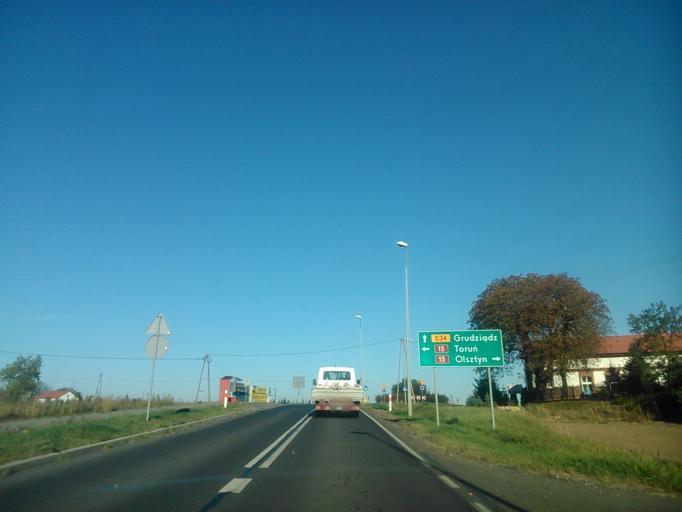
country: PL
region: Kujawsko-Pomorskie
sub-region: Powiat golubsko-dobrzynski
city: Golub-Dobrzyn
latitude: 53.1877
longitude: 19.0439
